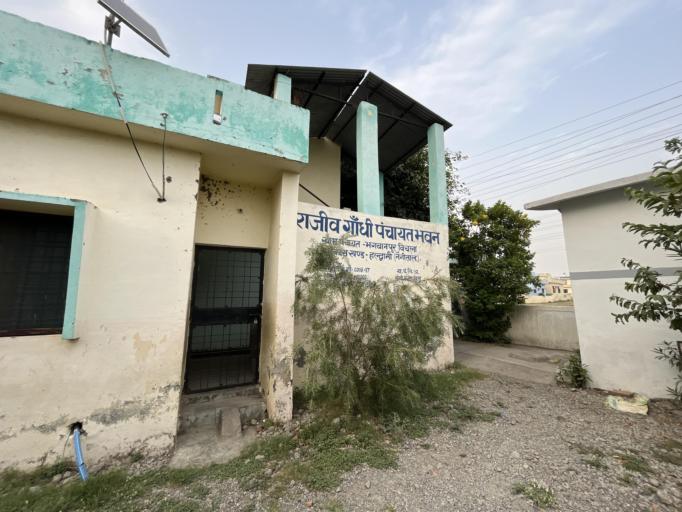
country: IN
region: Uttarakhand
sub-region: Naini Tal
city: Haldwani
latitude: 29.2194
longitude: 79.4751
